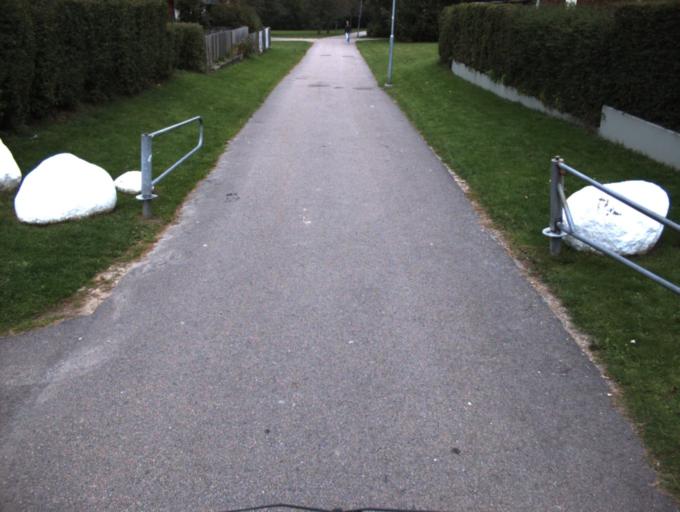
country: SE
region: Skane
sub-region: Helsingborg
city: Odakra
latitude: 56.0949
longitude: 12.7562
